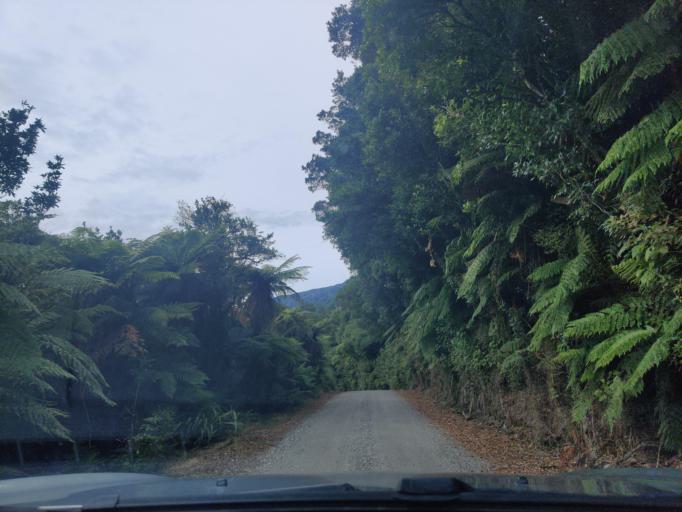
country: NZ
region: West Coast
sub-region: Westland District
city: Hokitika
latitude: -43.2914
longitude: 170.4055
